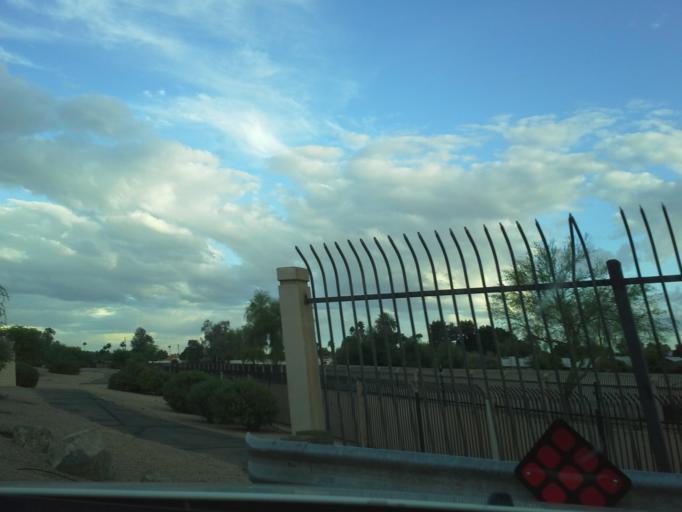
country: US
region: Arizona
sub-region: Maricopa County
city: Phoenix
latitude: 33.5455
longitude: -112.0551
